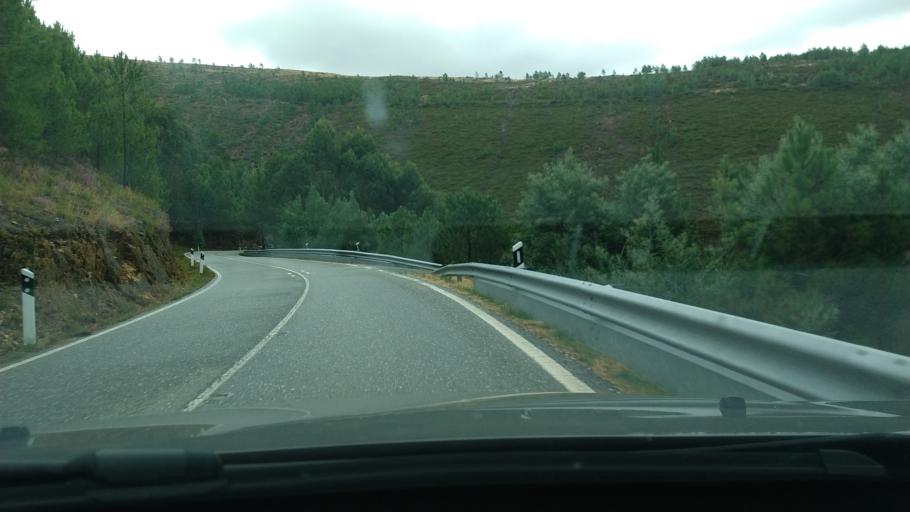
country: PT
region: Castelo Branco
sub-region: Covilha
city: Covilha
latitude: 40.2425
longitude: -7.6738
